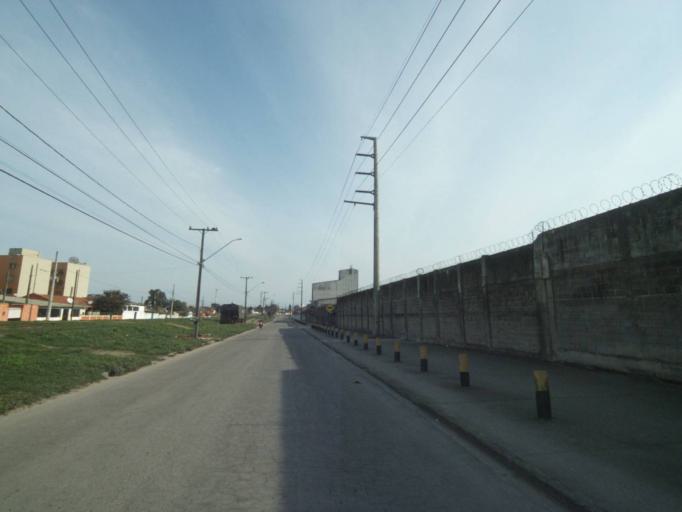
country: BR
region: Parana
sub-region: Paranagua
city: Paranagua
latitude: -25.5316
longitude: -48.5316
